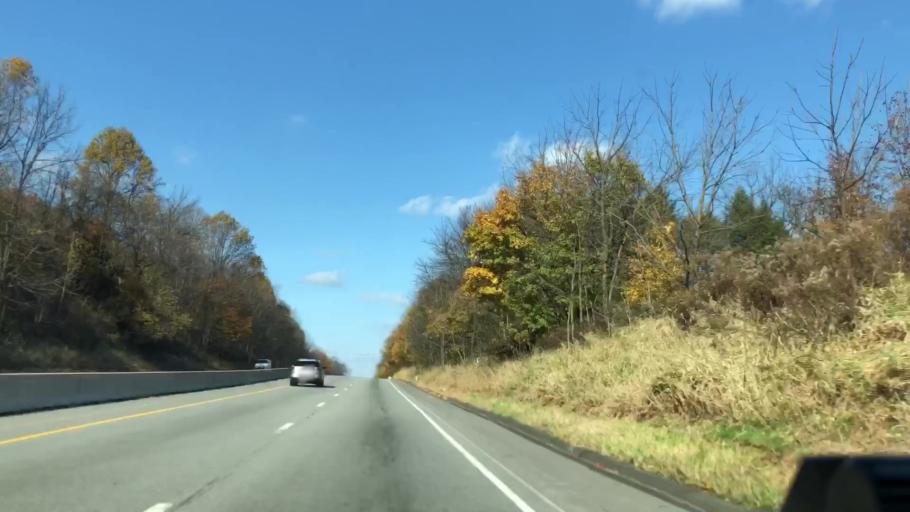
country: US
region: Pennsylvania
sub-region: Montgomery County
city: Halfway House
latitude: 40.2994
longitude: -75.6362
